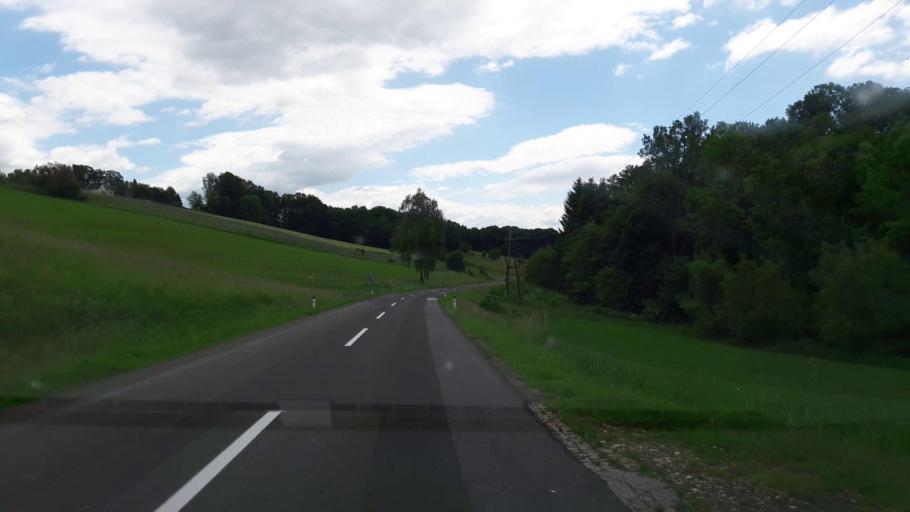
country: AT
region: Styria
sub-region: Politischer Bezirk Hartberg-Fuerstenfeld
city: Soechau
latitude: 47.0451
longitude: 16.0153
